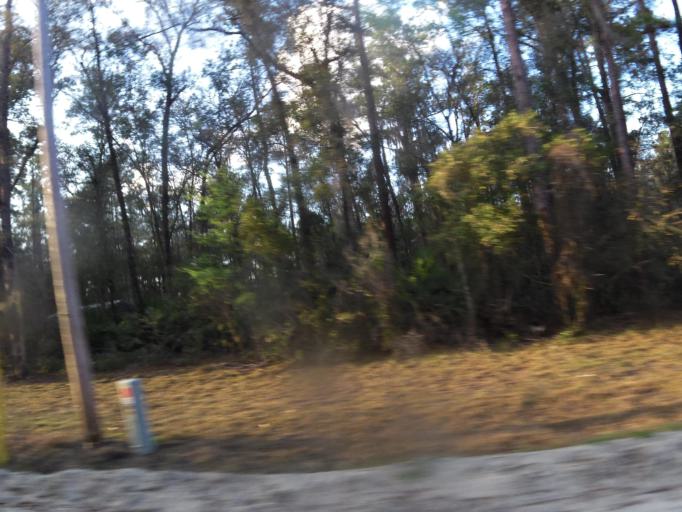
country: US
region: Florida
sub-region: Putnam County
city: Interlachen
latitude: 29.7804
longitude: -81.8425
